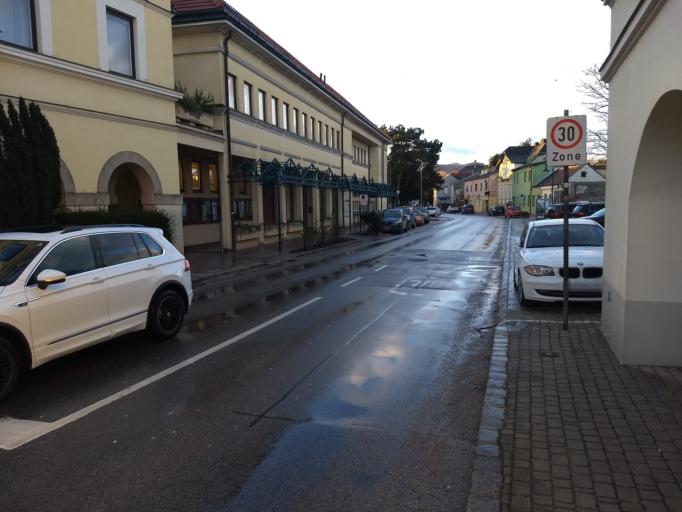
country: AT
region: Lower Austria
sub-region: Politischer Bezirk Korneuburg
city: Langenzersdorf
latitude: 48.3092
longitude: 16.3579
